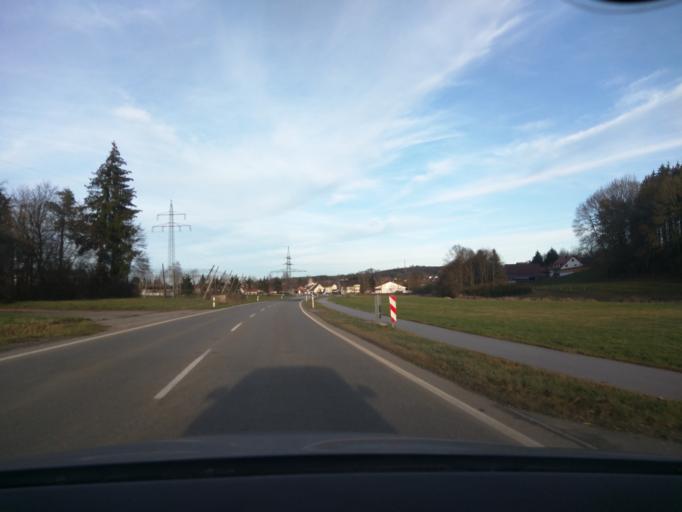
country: DE
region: Bavaria
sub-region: Upper Bavaria
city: Au in der Hallertau
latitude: 48.5524
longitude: 11.7307
